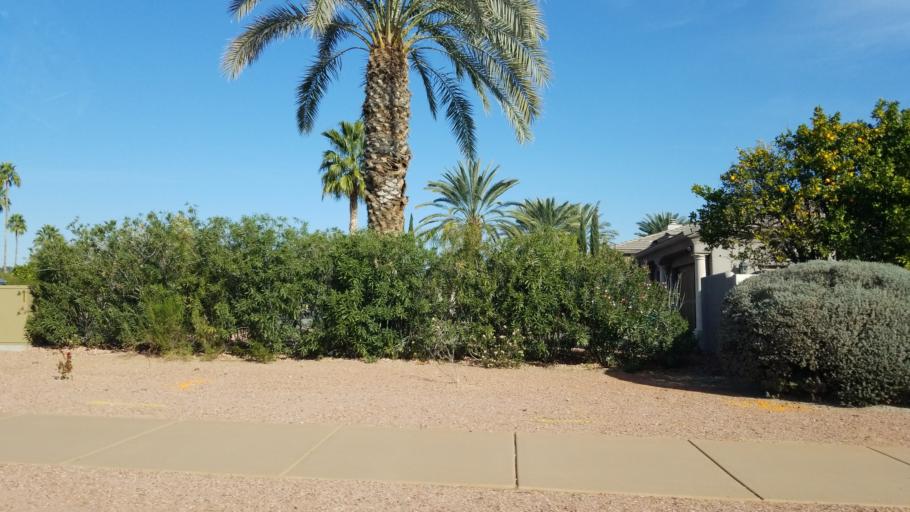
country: US
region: Arizona
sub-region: Maricopa County
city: Paradise Valley
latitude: 33.5676
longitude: -111.9369
